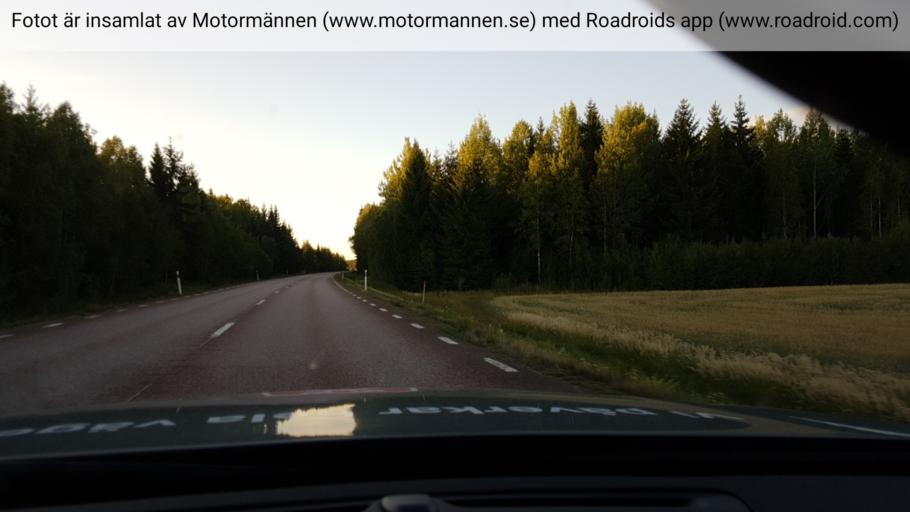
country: SE
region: OErebro
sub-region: Karlskoga Kommun
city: Karlskoga
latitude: 59.4143
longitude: 14.4266
